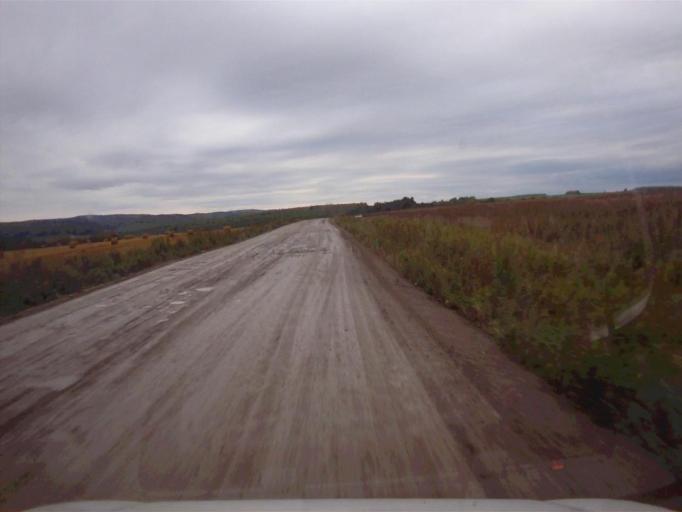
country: RU
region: Sverdlovsk
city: Mikhaylovsk
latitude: 56.1811
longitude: 59.1894
